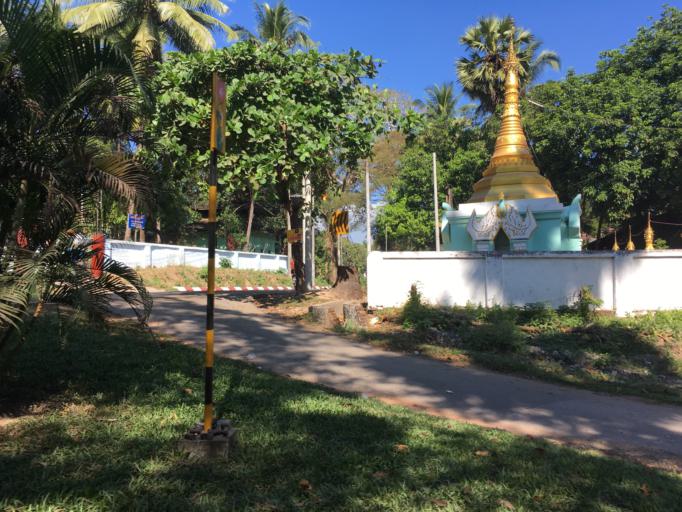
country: MM
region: Mon
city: Mawlamyine
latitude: 16.4902
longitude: 97.6303
